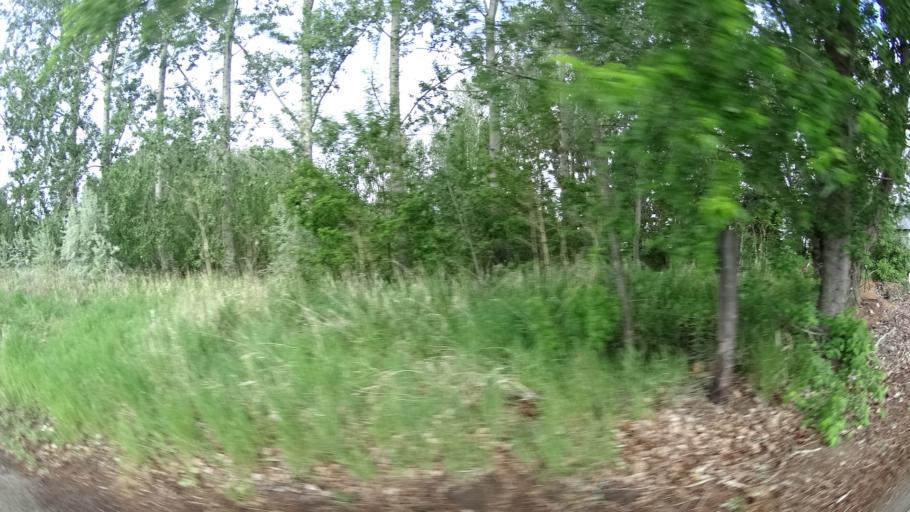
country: US
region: Idaho
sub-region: Ada County
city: Star
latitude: 43.6990
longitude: -116.5128
